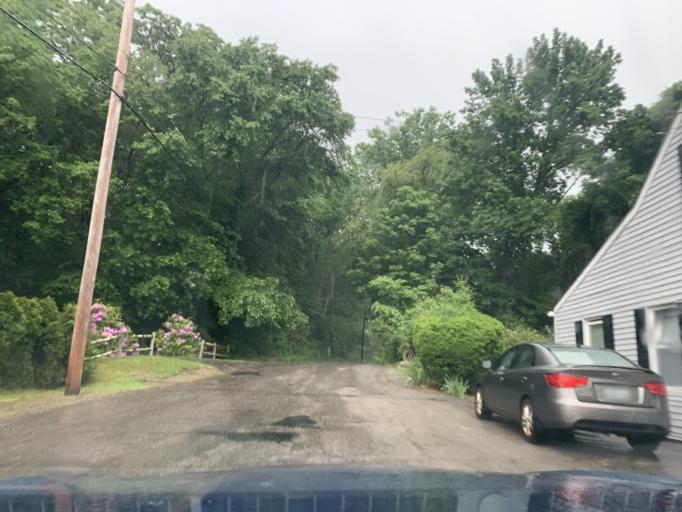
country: US
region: Rhode Island
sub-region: Kent County
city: West Warwick
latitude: 41.7307
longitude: -71.5510
